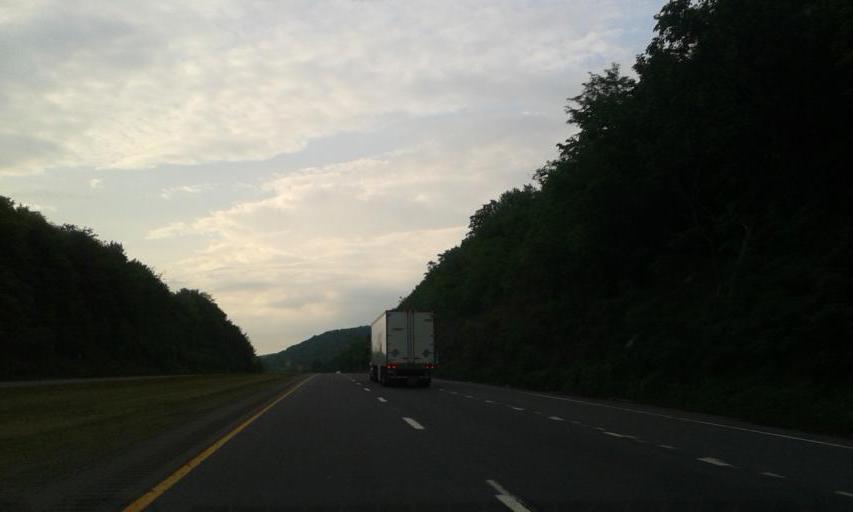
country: US
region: Pennsylvania
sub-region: Susquehanna County
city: Hallstead
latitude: 41.9701
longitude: -75.7396
